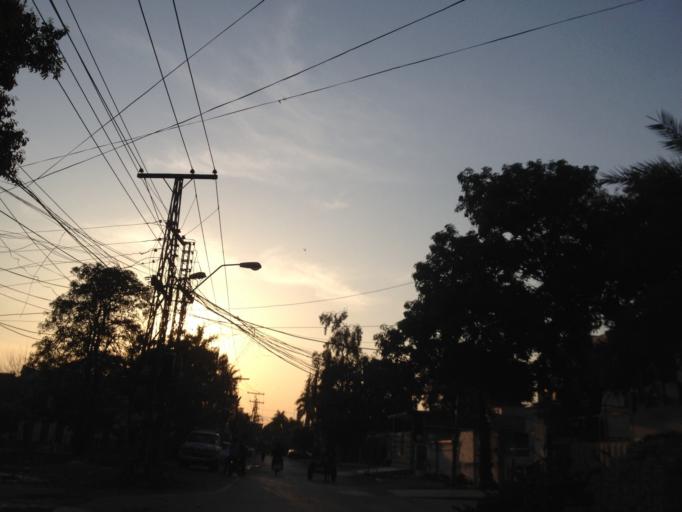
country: PK
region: Punjab
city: Lahore
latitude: 31.5002
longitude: 74.3292
